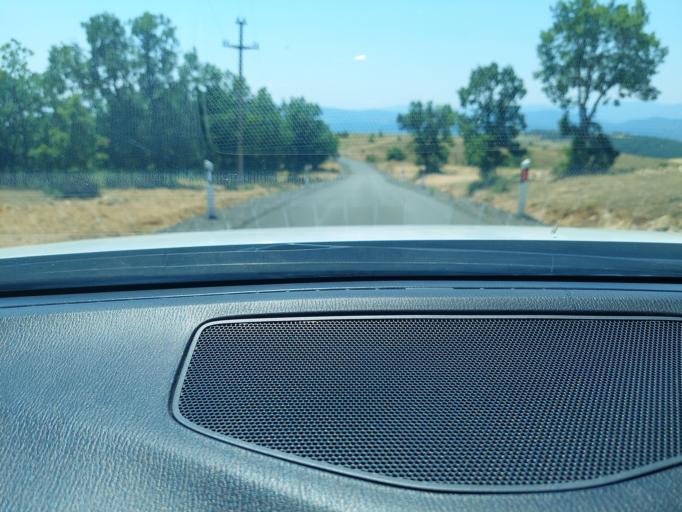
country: MK
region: Radovis
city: Radovish
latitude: 41.6654
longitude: 22.4082
